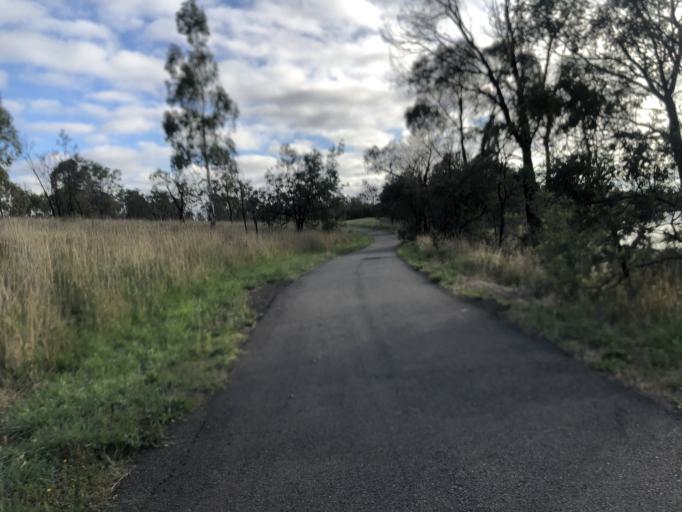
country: AU
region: New South Wales
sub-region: Orange Municipality
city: Orange
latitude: -33.3279
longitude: 149.0863
